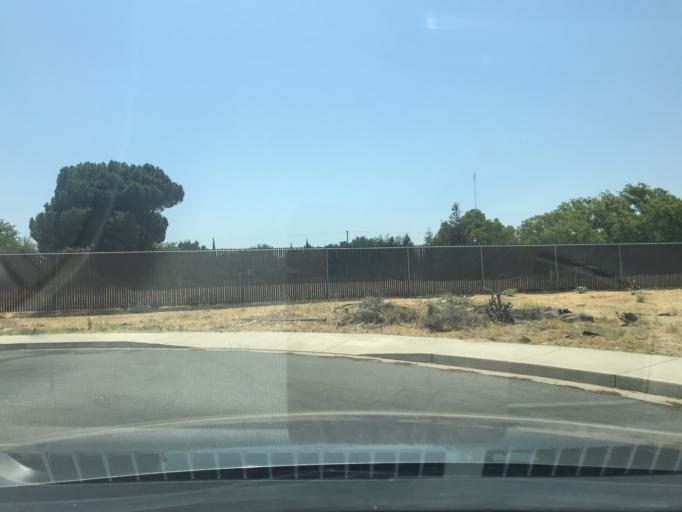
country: US
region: California
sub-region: Merced County
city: Winton
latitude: 37.3725
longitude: -120.6007
